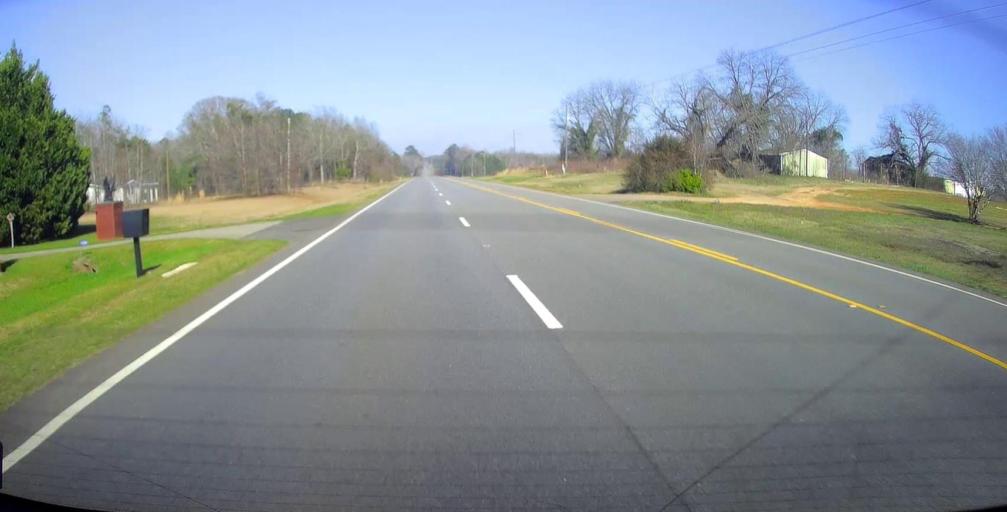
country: US
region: Georgia
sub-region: Macon County
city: Montezuma
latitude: 32.3222
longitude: -83.8853
